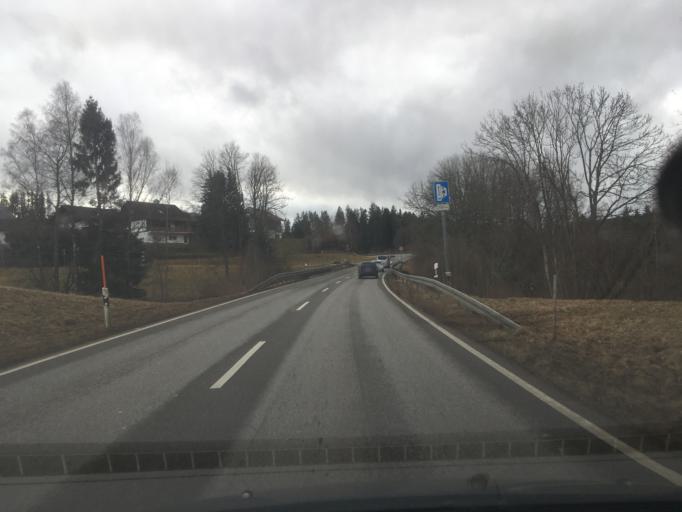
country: DE
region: Baden-Wuerttemberg
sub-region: Freiburg Region
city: Hausern
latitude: 47.7513
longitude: 8.1651
